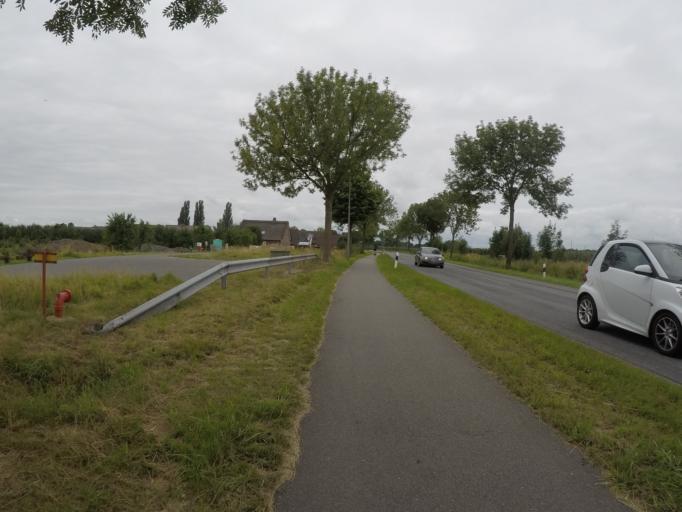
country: DE
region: Lower Saxony
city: Jork
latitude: 53.5380
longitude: 9.7015
